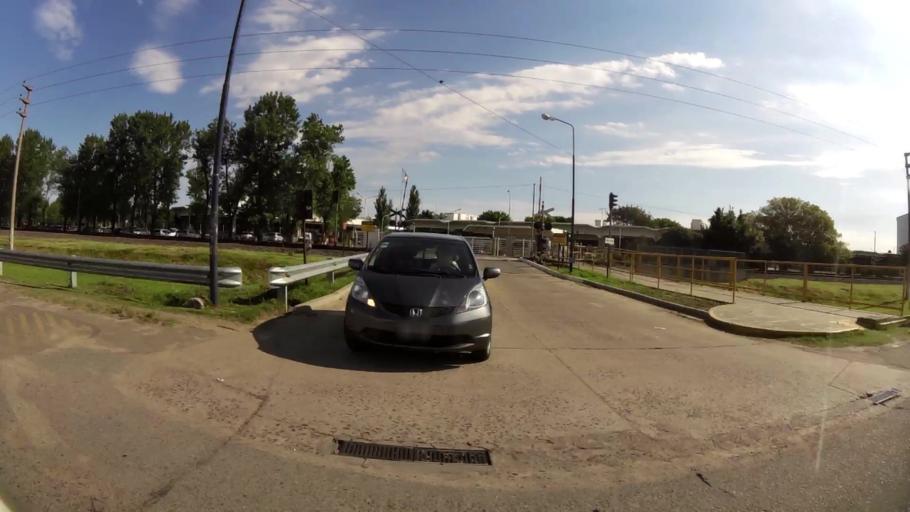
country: AR
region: Buenos Aires
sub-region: Partido de Merlo
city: Merlo
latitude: -34.6614
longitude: -58.7467
